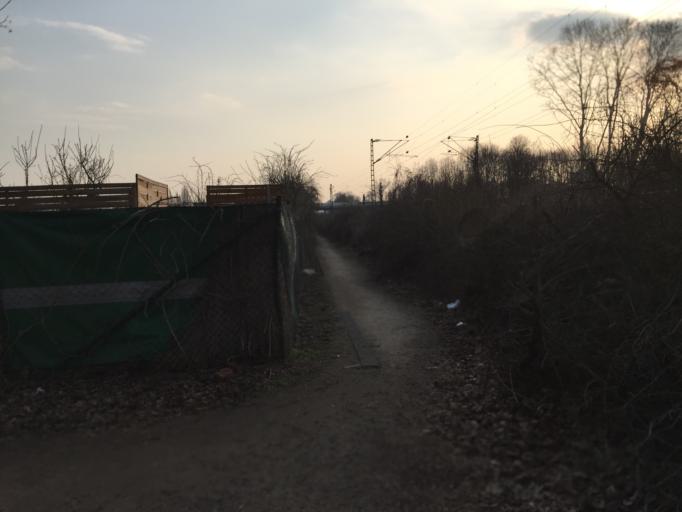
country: DE
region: Hesse
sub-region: Regierungsbezirk Darmstadt
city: Frankfurt am Main
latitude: 50.1370
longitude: 8.6400
